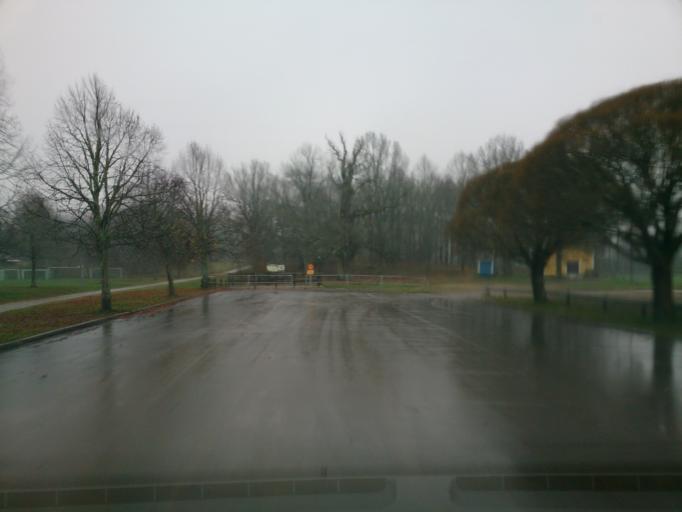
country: SE
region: OEstergoetland
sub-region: Atvidabergs Kommun
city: Atvidaberg
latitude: 58.1904
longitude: 15.9963
